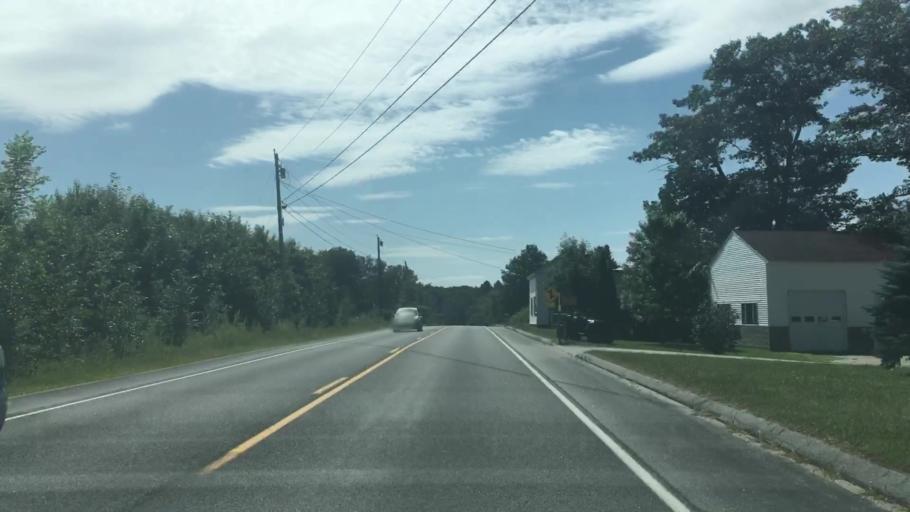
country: US
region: Maine
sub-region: Androscoggin County
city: Lisbon
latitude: 44.0614
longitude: -70.0855
